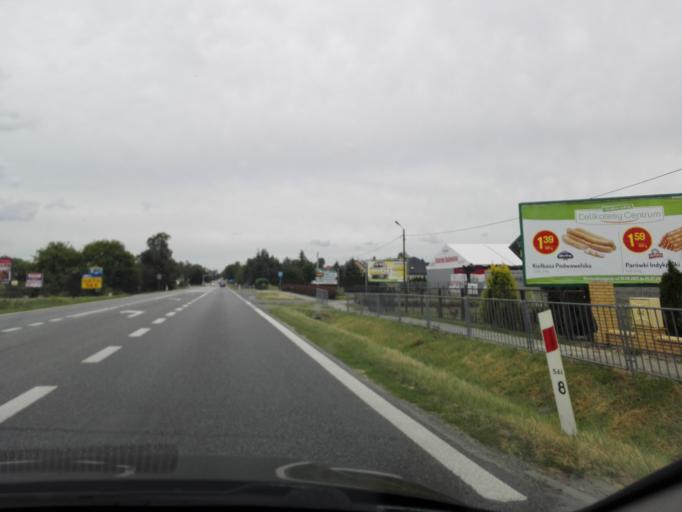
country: PL
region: Lublin Voivodeship
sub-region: Powiat pulawski
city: Konskowola
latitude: 51.4104
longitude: 22.0370
